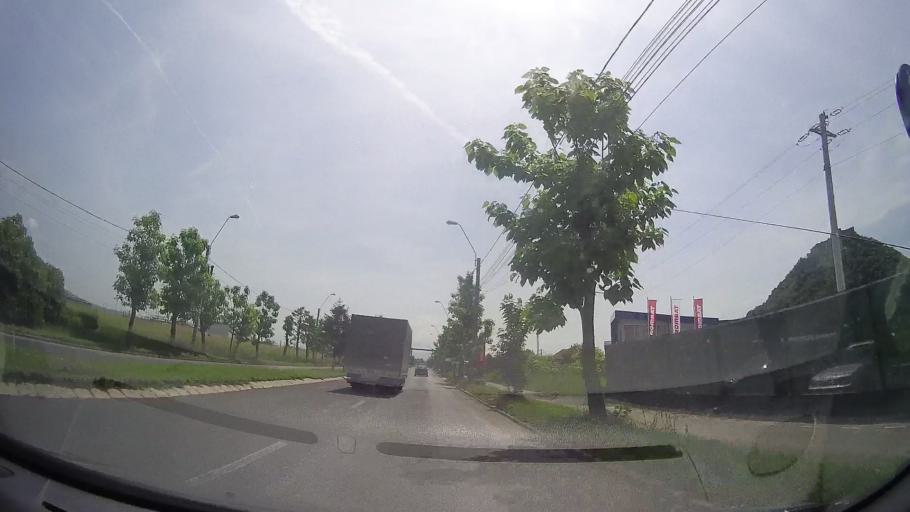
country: RO
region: Hunedoara
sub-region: Municipiul Deva
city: Deva
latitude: 45.8963
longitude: 22.8963
